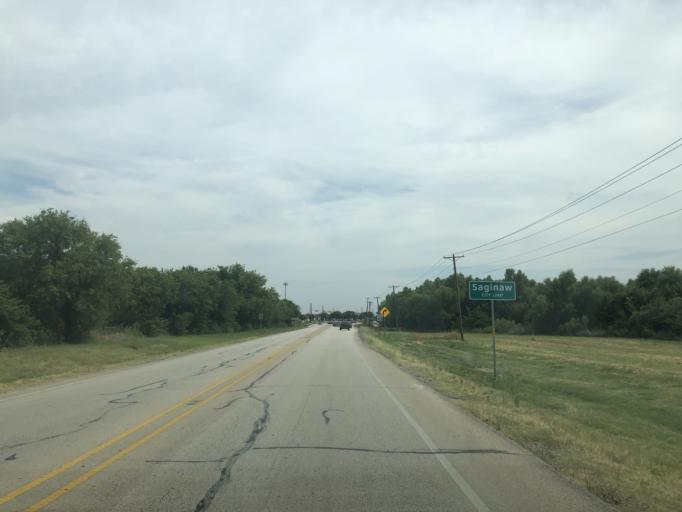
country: US
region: Texas
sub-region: Tarrant County
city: Blue Mound
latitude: 32.8863
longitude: -97.3440
